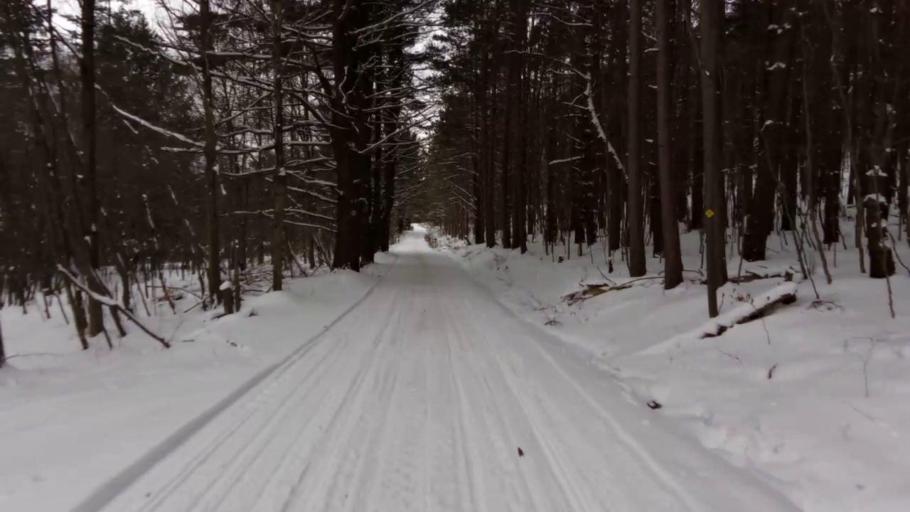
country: US
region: Pennsylvania
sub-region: McKean County
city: Bradford
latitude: 42.0258
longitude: -78.7219
